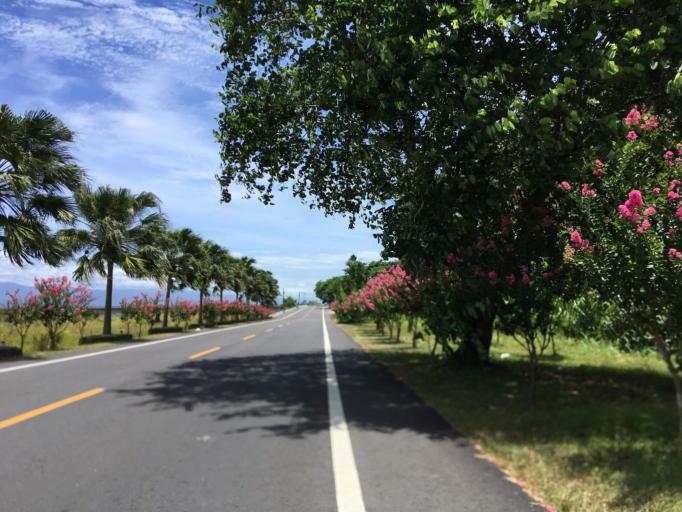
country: TW
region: Taiwan
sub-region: Yilan
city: Yilan
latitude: 24.6485
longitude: 121.7244
